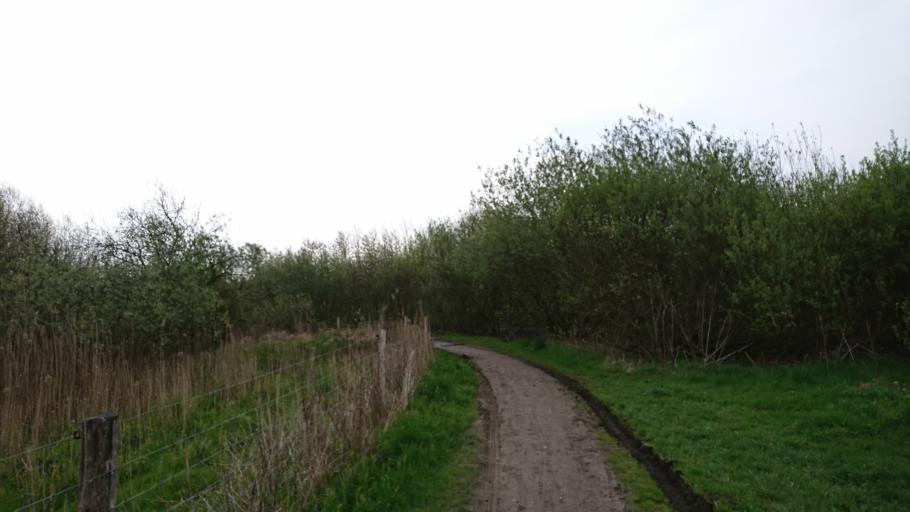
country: DK
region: Capital Region
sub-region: Herlev Kommune
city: Herlev
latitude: 55.7316
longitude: 12.4021
